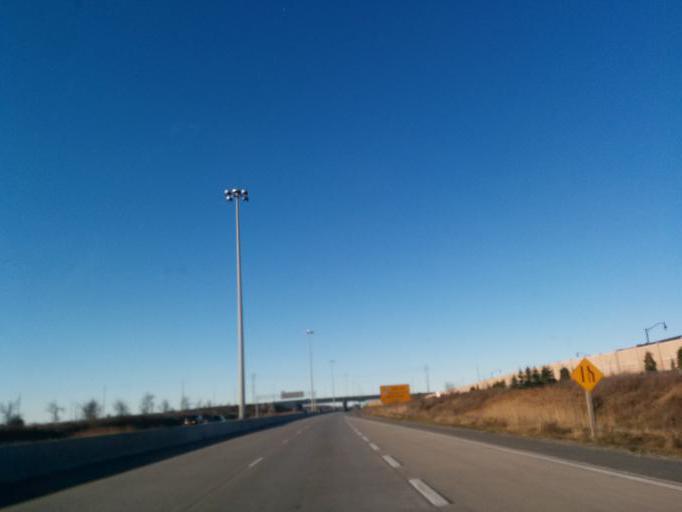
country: CA
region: Ontario
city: Brampton
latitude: 43.7449
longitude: -79.7857
